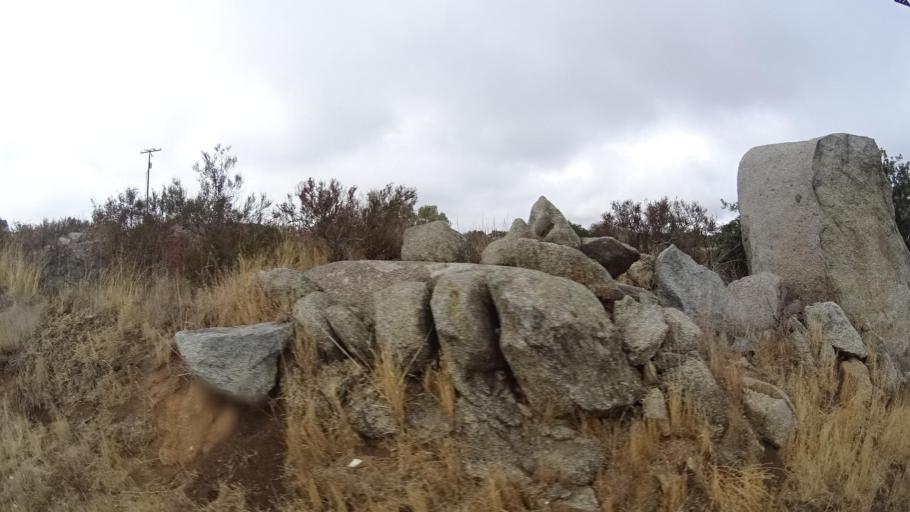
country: MX
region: Baja California
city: Tecate
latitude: 32.6010
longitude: -116.5820
